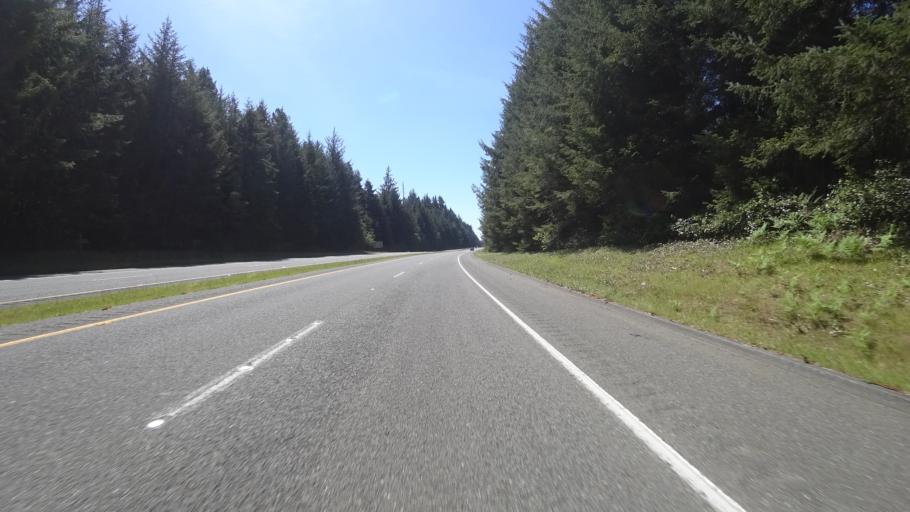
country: US
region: California
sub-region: Humboldt County
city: Westhaven-Moonstone
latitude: 41.1205
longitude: -124.1512
